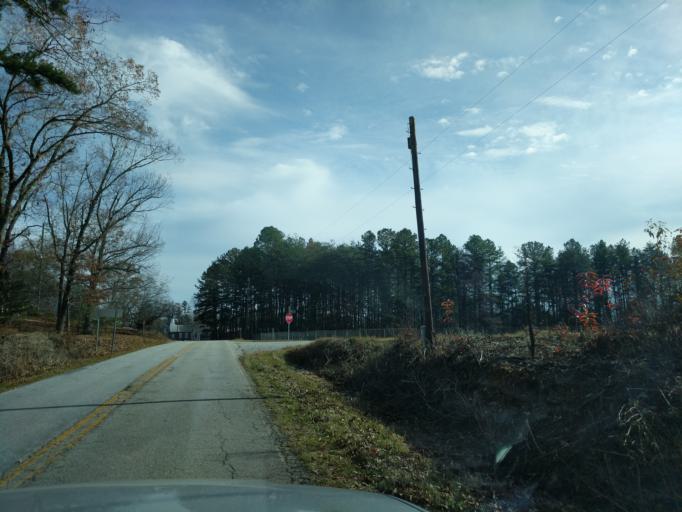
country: US
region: South Carolina
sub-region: Oconee County
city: Walhalla
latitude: 34.8359
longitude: -83.0561
